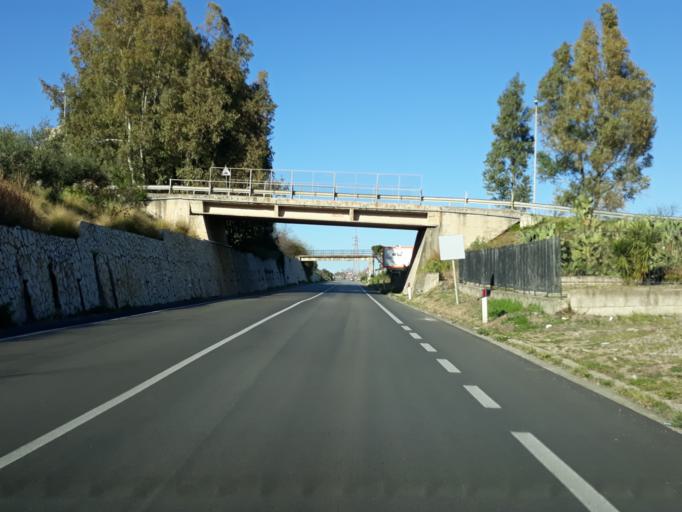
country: IT
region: Sicily
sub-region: Palermo
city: Misilmeri
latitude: 38.0361
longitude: 13.4594
